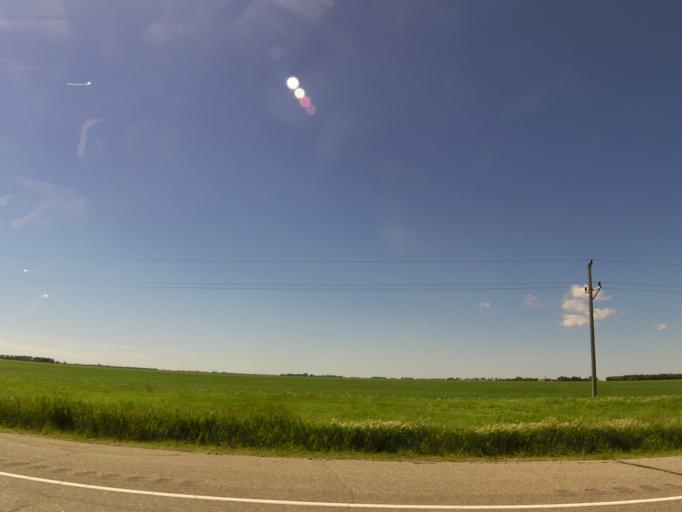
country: US
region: Minnesota
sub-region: Polk County
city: Crookston
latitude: 47.7603
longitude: -96.5303
